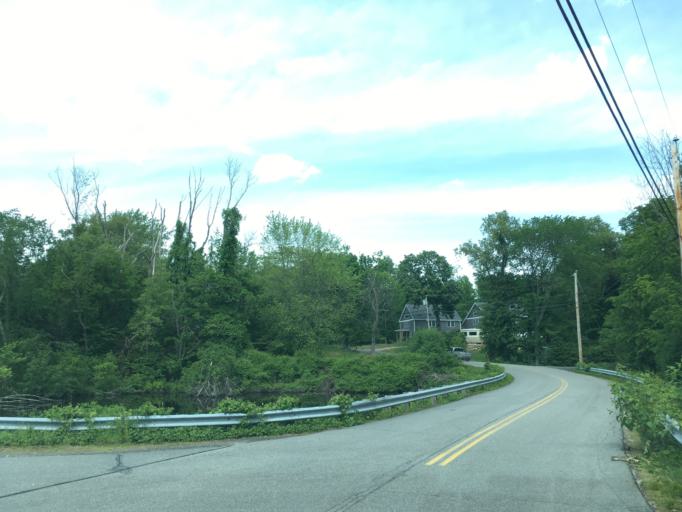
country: US
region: New Hampshire
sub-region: Rockingham County
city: Stratham Station
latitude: 43.0312
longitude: -70.8718
